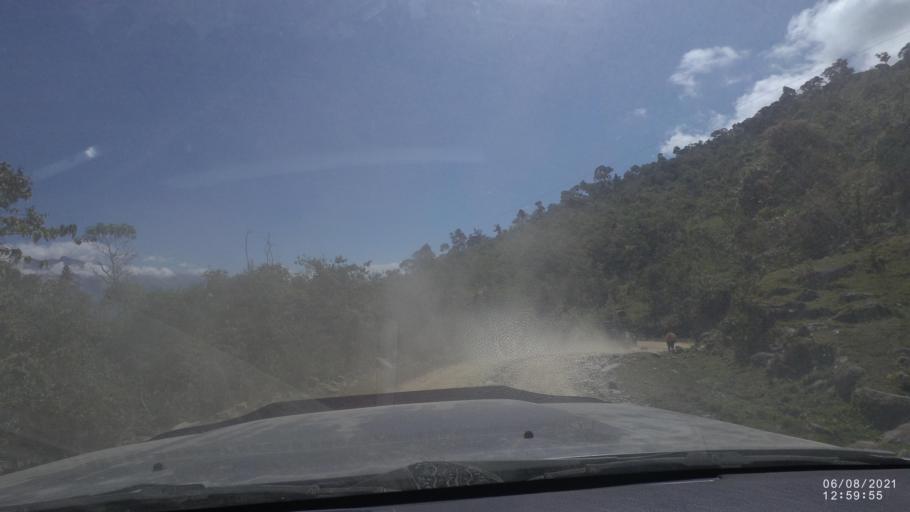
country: BO
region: Cochabamba
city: Colchani
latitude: -16.7488
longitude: -66.6882
